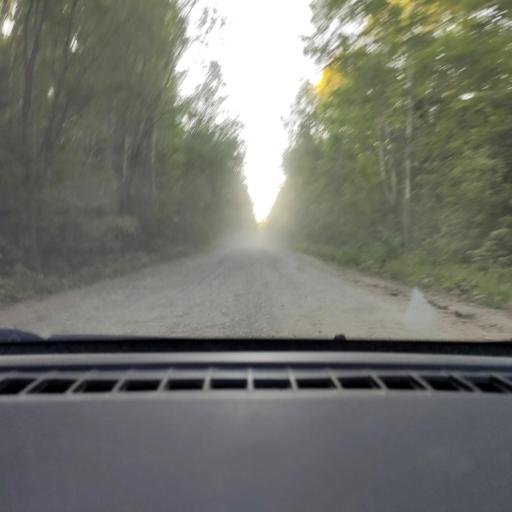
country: RU
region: Perm
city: Polazna
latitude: 58.1268
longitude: 56.4368
